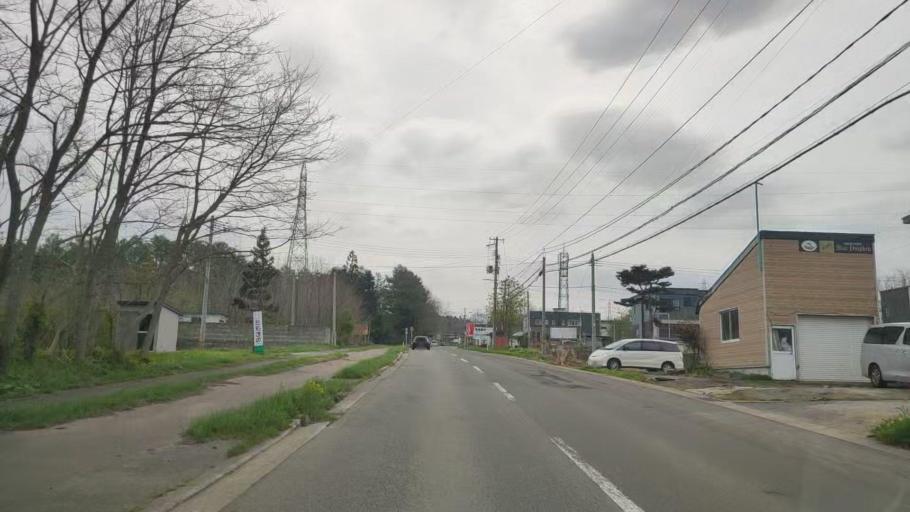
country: JP
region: Aomori
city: Aomori Shi
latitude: 40.7695
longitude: 140.7995
